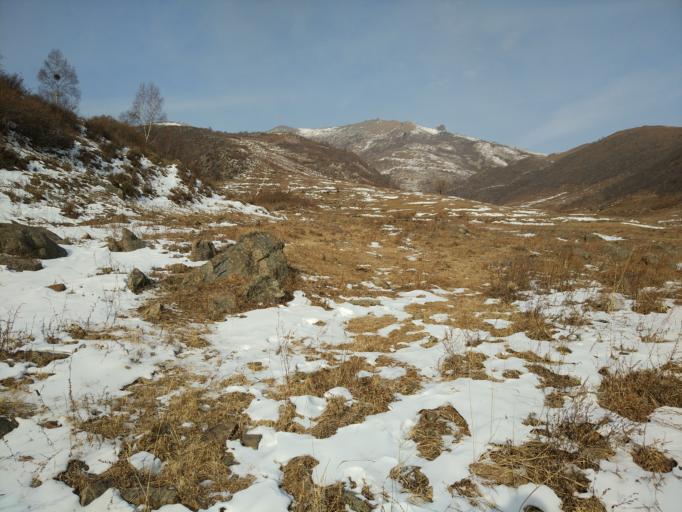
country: CN
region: Hebei
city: Xiwanzi
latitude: 40.8554
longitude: 115.4578
